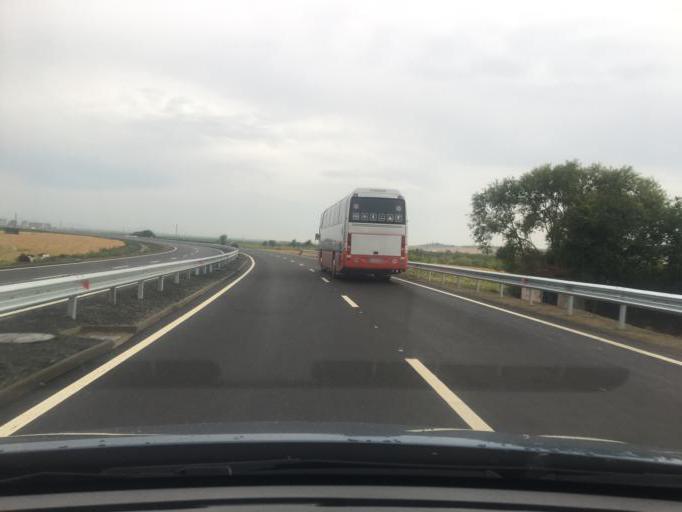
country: BG
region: Burgas
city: Aheloy
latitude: 42.6526
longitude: 27.6382
